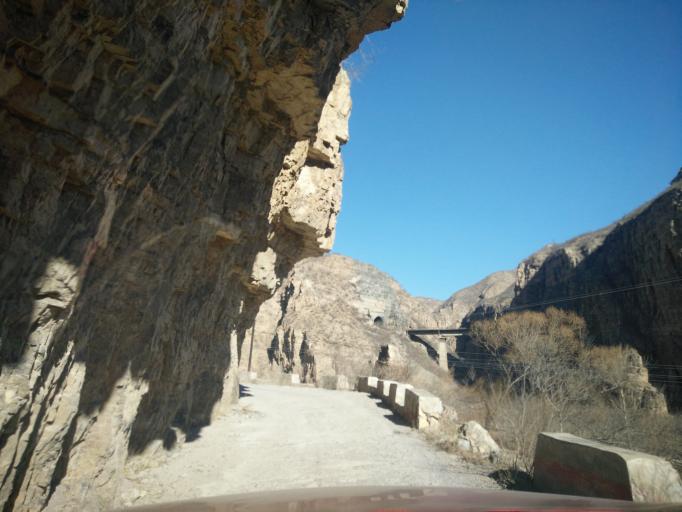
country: CN
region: Beijing
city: Yanjiatai
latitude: 40.1677
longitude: 115.6636
